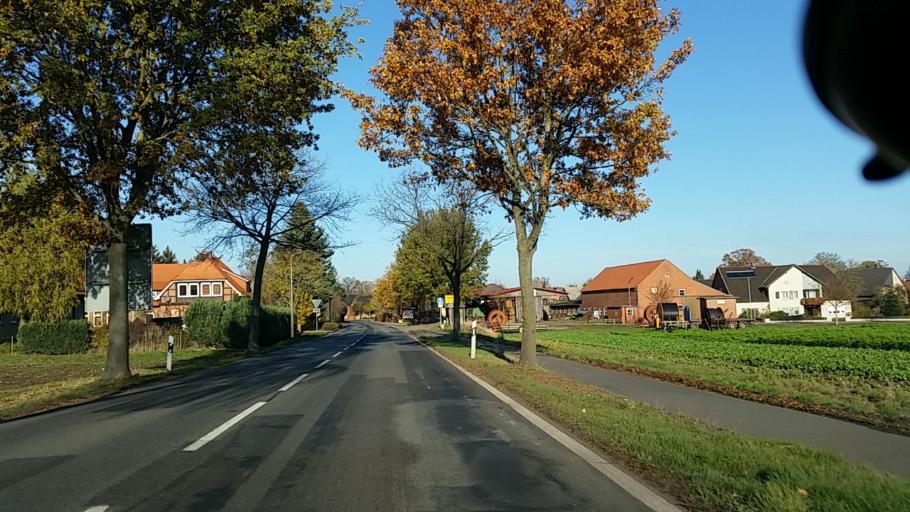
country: DE
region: Lower Saxony
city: Tulau
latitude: 52.6444
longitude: 10.8683
